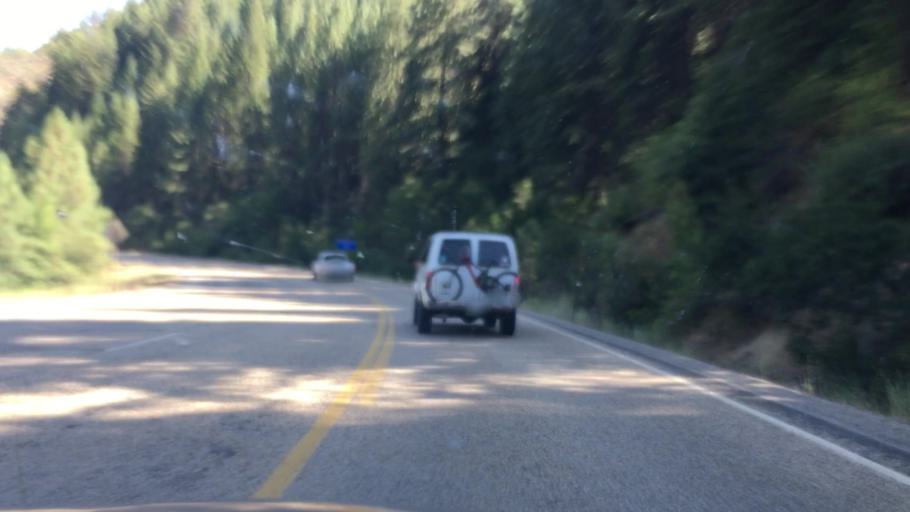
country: US
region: Idaho
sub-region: Boise County
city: Idaho City
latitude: 44.1189
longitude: -116.1122
